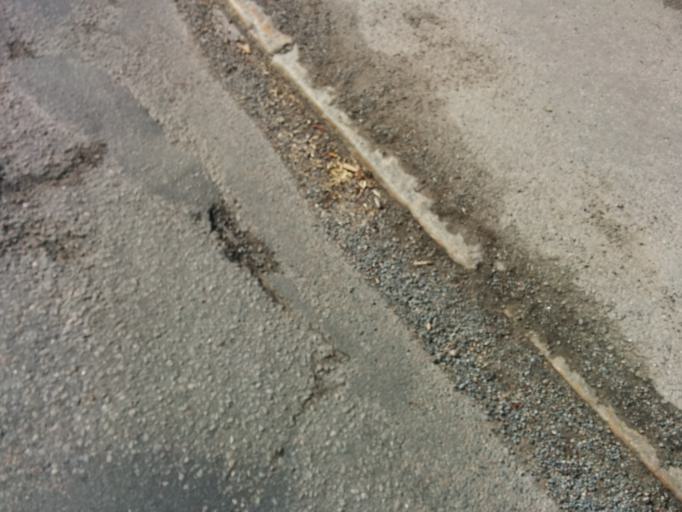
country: SE
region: Stockholm
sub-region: Solna Kommun
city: Solna
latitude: 59.3082
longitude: 17.9978
